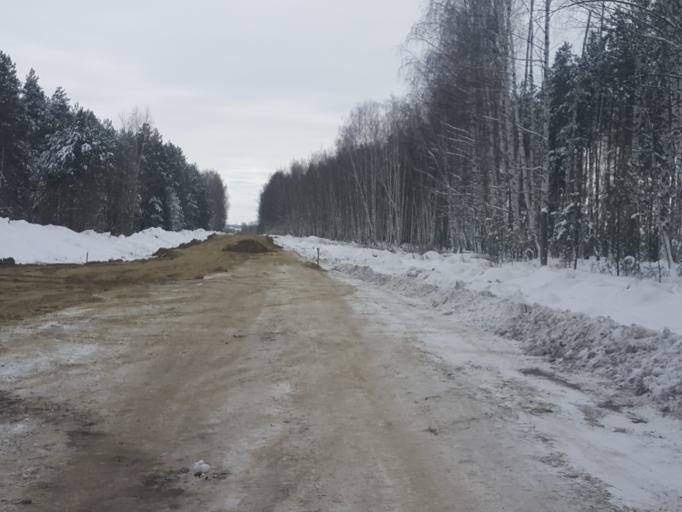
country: RU
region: Tambov
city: Platonovka
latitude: 52.8842
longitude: 41.8624
